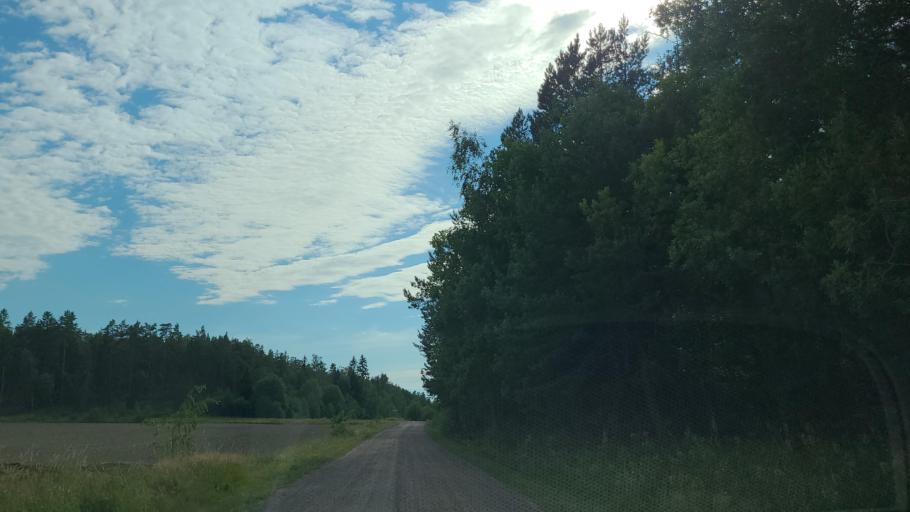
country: FI
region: Varsinais-Suomi
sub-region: Turku
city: Rymaettylae
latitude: 60.2881
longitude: 21.9277
